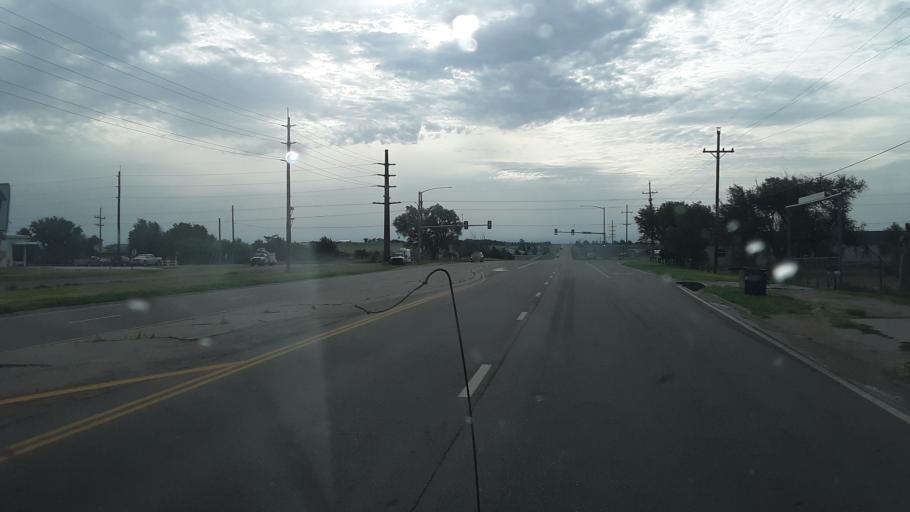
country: US
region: Kansas
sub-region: Finney County
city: Garden City
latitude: 37.9602
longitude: -100.8123
